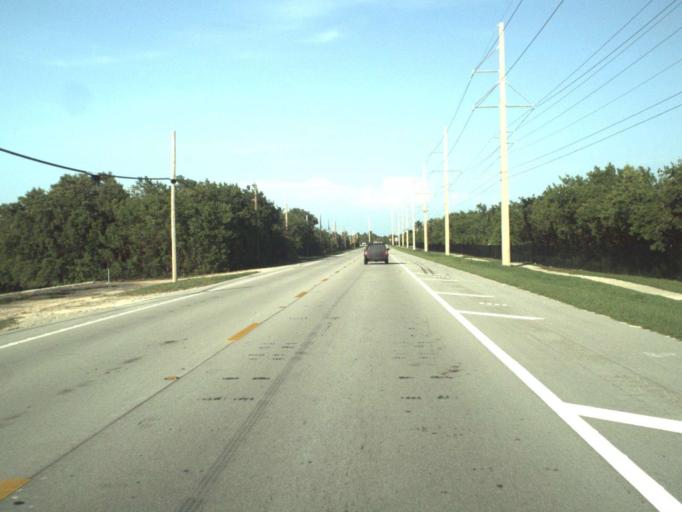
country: US
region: Florida
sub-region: Monroe County
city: Islamorada
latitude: 24.8085
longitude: -80.8354
